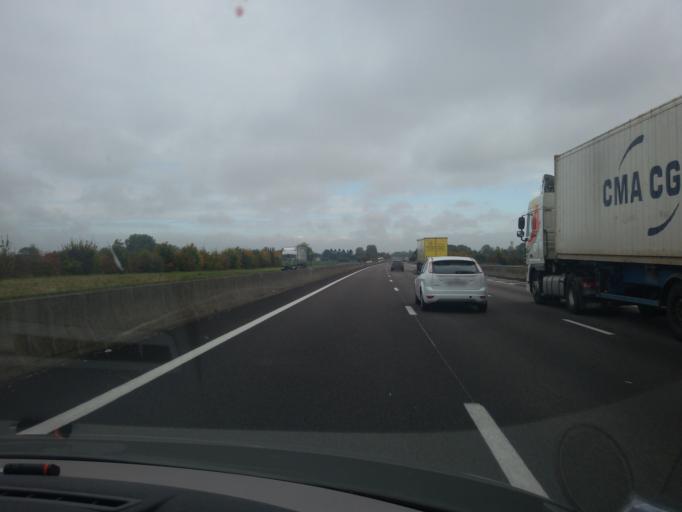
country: FR
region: Haute-Normandie
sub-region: Departement de l'Eure
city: Hauville
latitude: 49.3719
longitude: 0.6890
